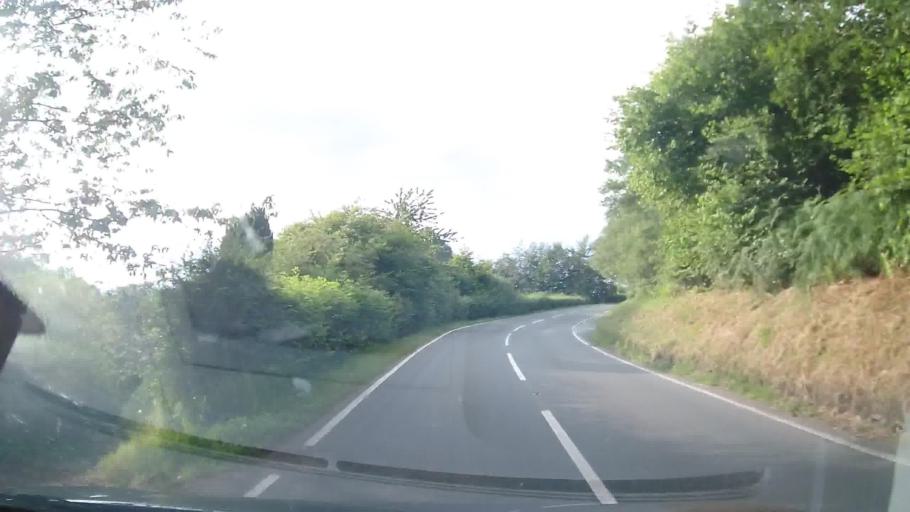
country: GB
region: Wales
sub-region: Gwynedd
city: Bala
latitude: 52.9037
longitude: -3.5181
